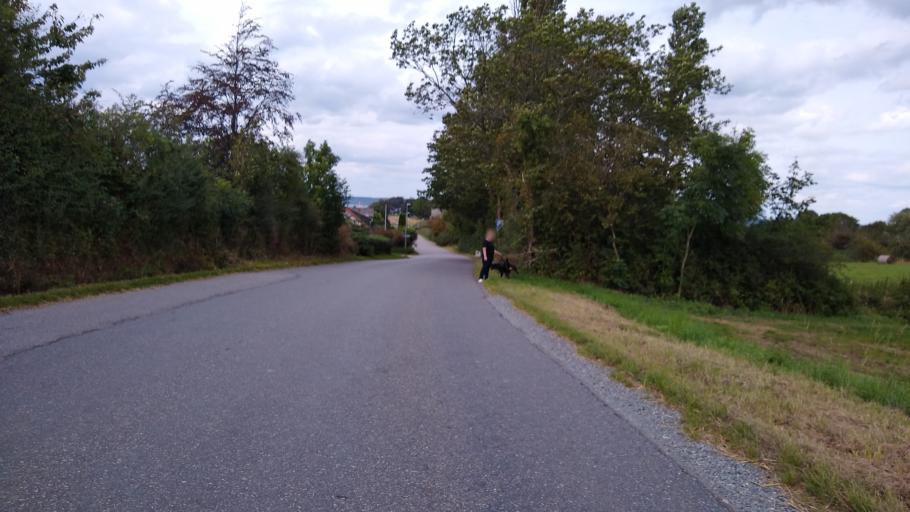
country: DK
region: South Denmark
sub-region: Fredericia Kommune
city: Fredericia
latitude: 55.6175
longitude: 9.7766
